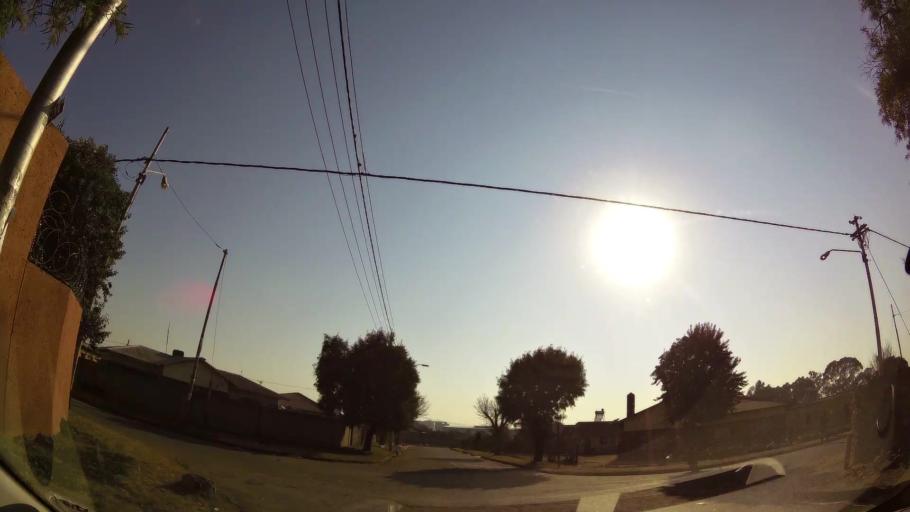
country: ZA
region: Gauteng
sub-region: City of Johannesburg Metropolitan Municipality
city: Modderfontein
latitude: -26.1567
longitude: 28.2032
